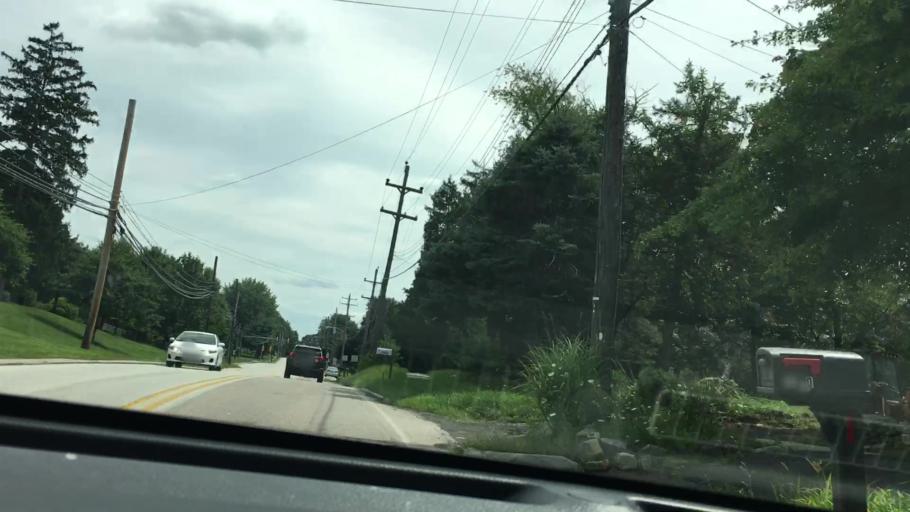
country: US
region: Pennsylvania
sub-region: Montgomery County
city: Hatboro
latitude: 40.1700
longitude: -75.0937
